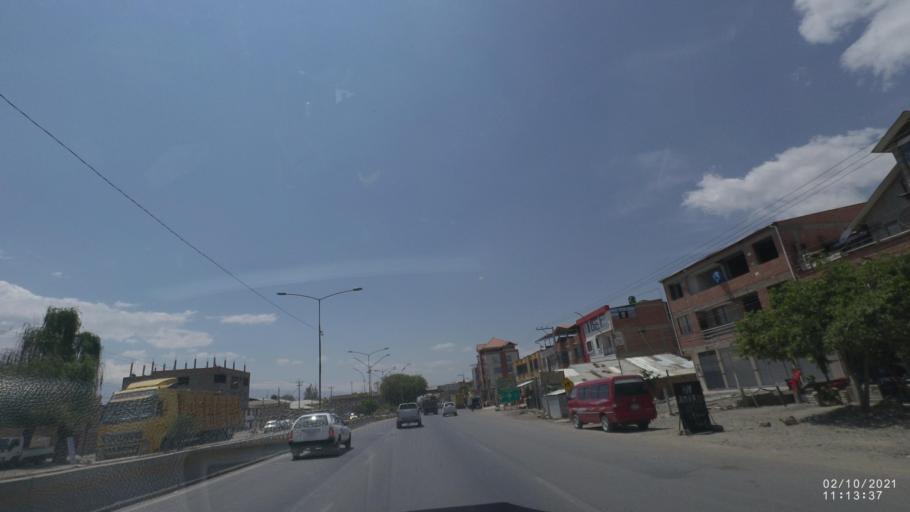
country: BO
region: Cochabamba
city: Sipe Sipe
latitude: -17.3962
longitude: -66.3185
